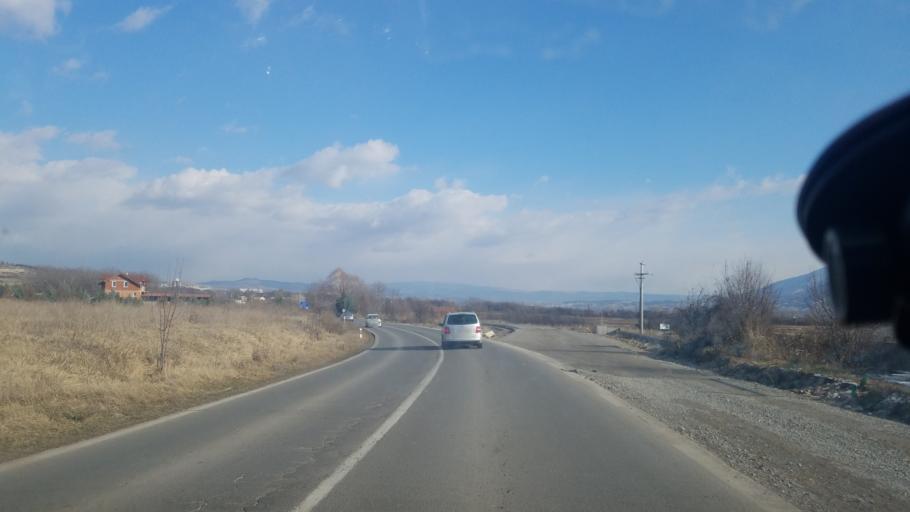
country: MK
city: Obleshevo
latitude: 41.8984
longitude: 22.3660
